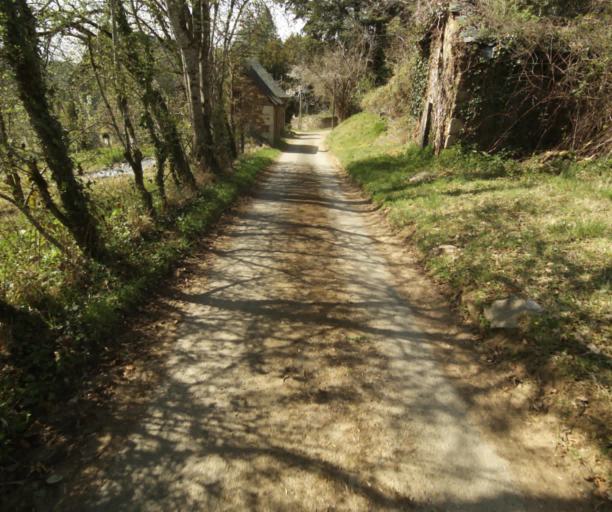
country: FR
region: Limousin
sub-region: Departement de la Correze
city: Naves
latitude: 45.3510
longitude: 1.7823
